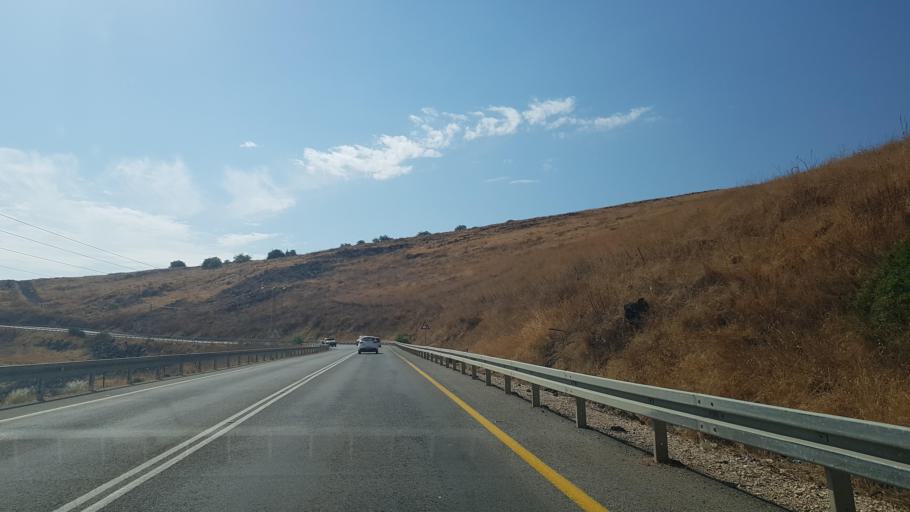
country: IL
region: Northern District
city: Rosh Pinna
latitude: 32.9127
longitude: 35.5621
